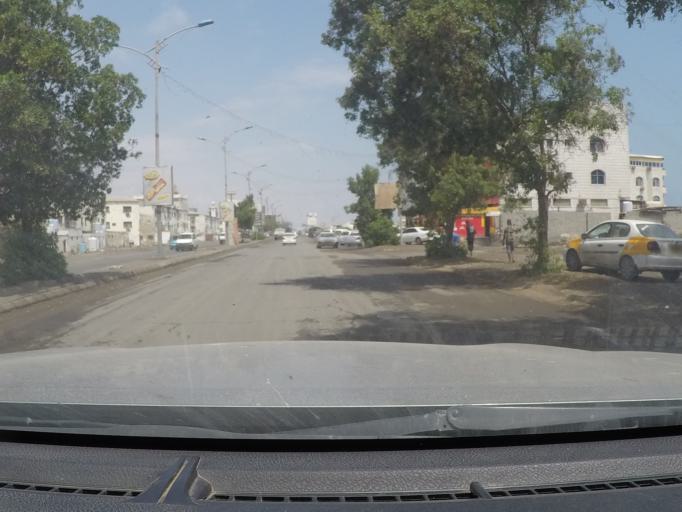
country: YE
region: Aden
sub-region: Khur Maksar
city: Khawr Maksar
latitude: 12.8130
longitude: 45.0418
